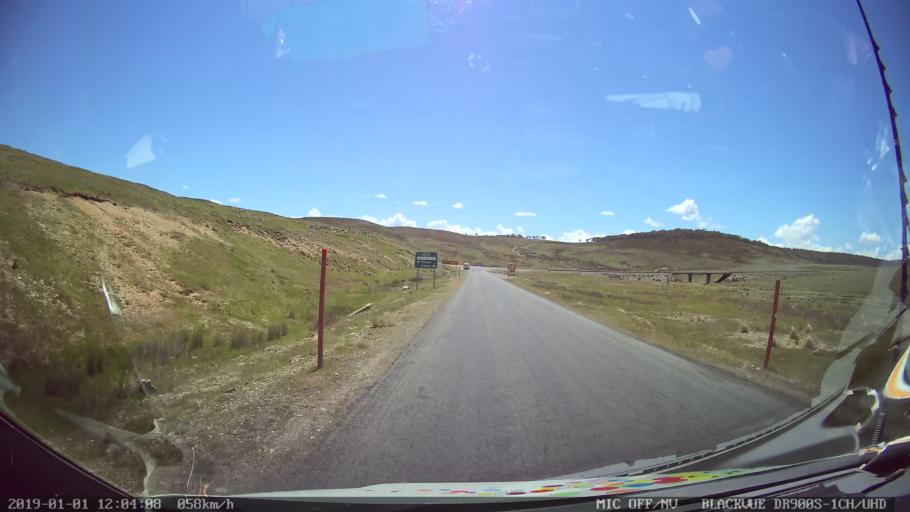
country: AU
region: New South Wales
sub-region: Snowy River
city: Jindabyne
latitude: -35.8681
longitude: 148.4936
